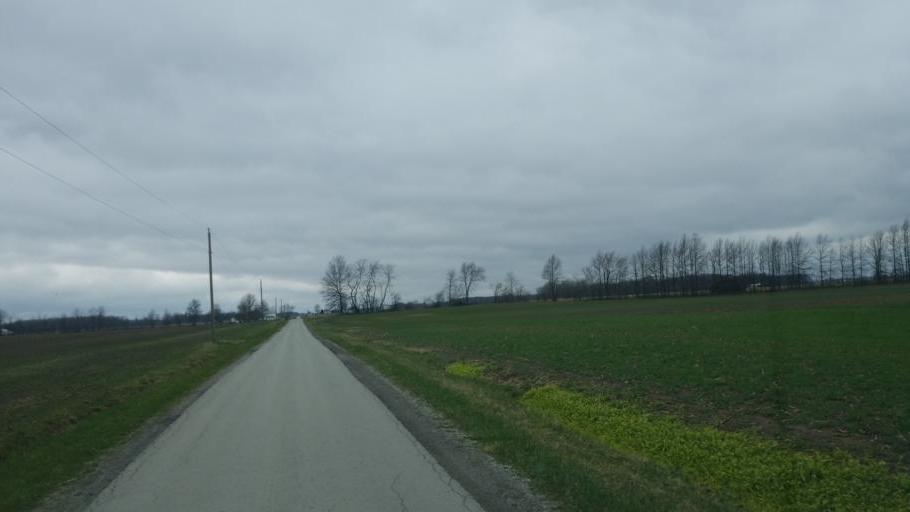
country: US
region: Ohio
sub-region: Hardin County
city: Forest
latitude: 40.7238
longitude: -83.4664
